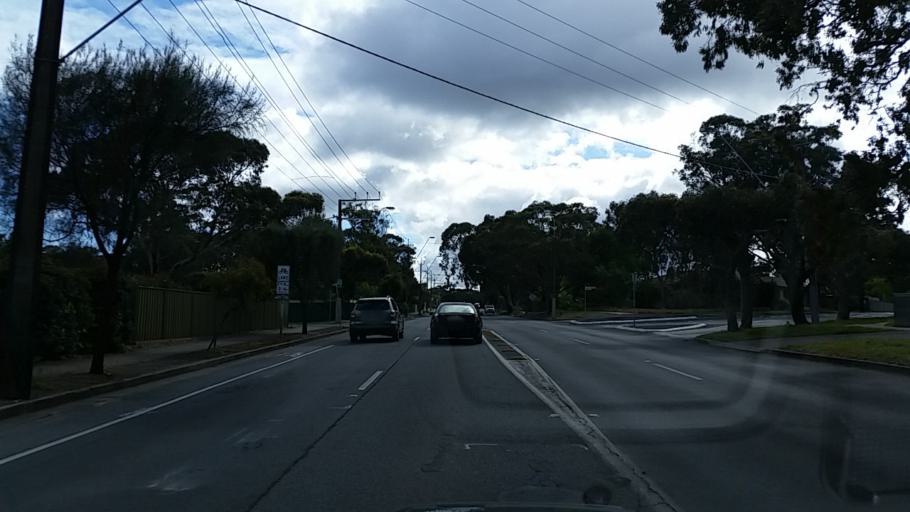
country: AU
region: South Australia
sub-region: Mitcham
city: Blackwood
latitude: -35.0254
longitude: 138.6047
